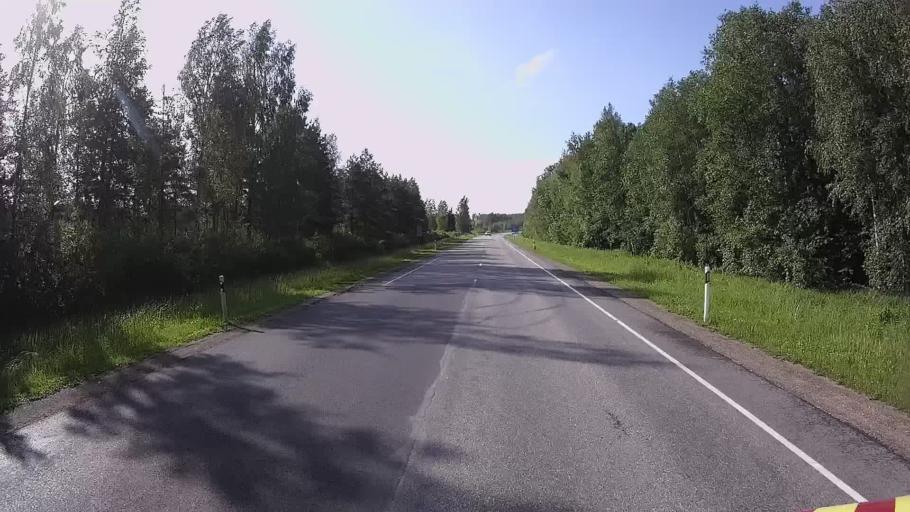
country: EE
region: Viljandimaa
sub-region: Viljandi linn
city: Viljandi
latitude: 58.3345
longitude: 25.5729
